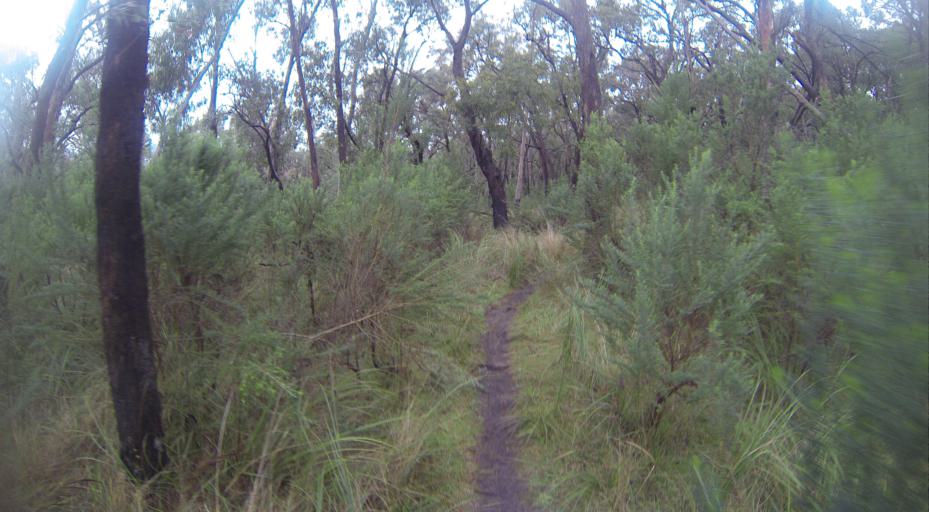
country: AU
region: Victoria
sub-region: Yarra Ranges
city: Belgrave South
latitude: -37.9300
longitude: 145.3267
